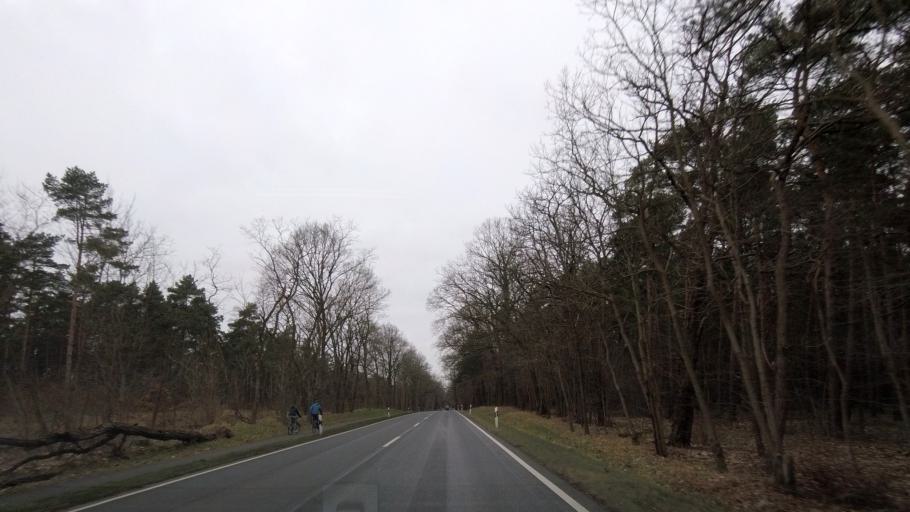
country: DE
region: Brandenburg
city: Treuenbrietzen
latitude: 52.0723
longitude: 12.8875
